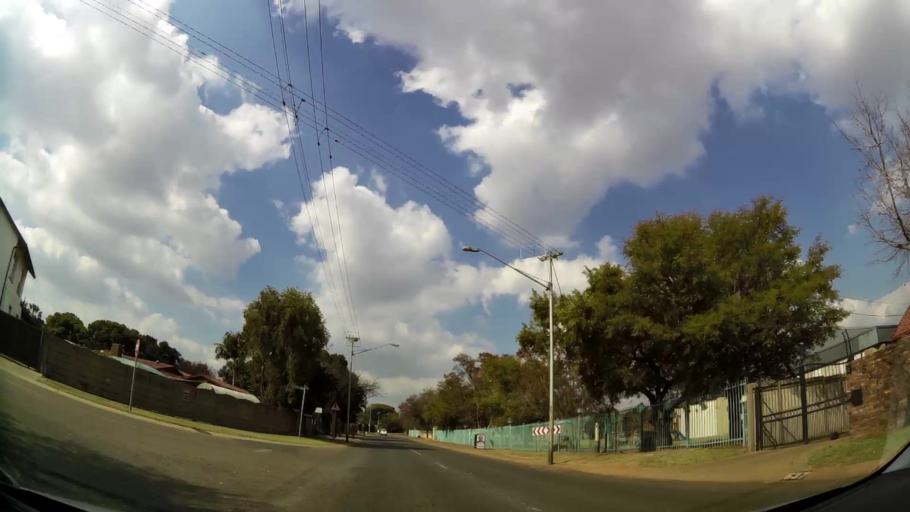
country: ZA
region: Gauteng
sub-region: City of Tshwane Metropolitan Municipality
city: Centurion
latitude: -25.8328
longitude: 28.2590
